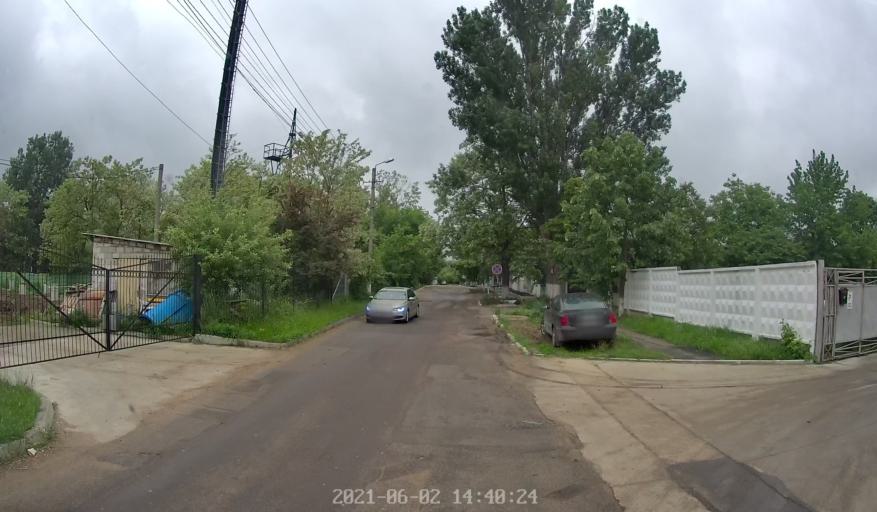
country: MD
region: Chisinau
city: Chisinau
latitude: 47.0455
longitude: 28.8010
